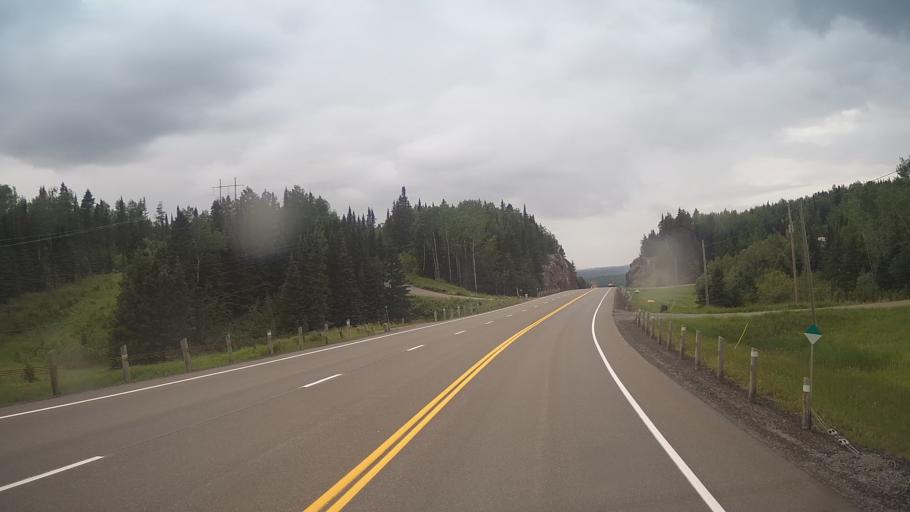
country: CA
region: Ontario
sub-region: Thunder Bay District
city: Thunder Bay
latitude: 48.5263
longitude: -89.5366
